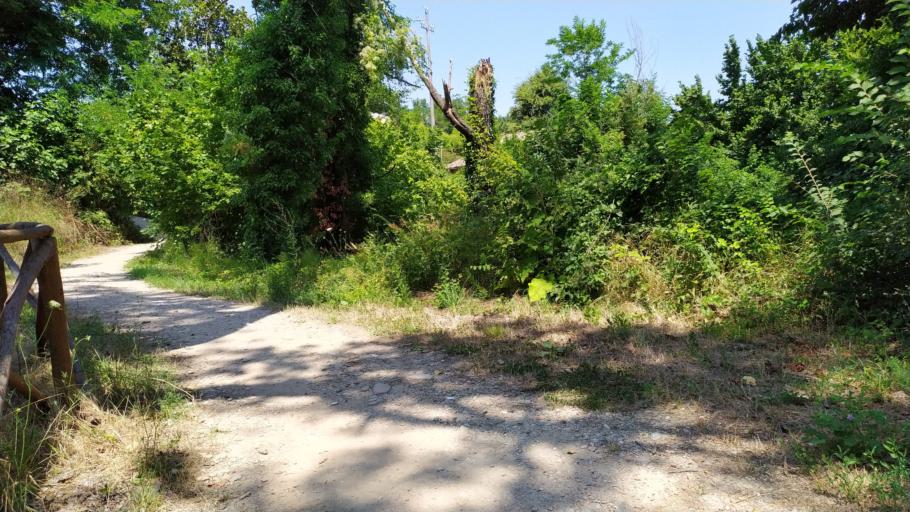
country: IT
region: Emilia-Romagna
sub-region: Forli-Cesena
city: Castrocaro Terme e Terra del Sole
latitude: 44.1926
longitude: 11.9736
